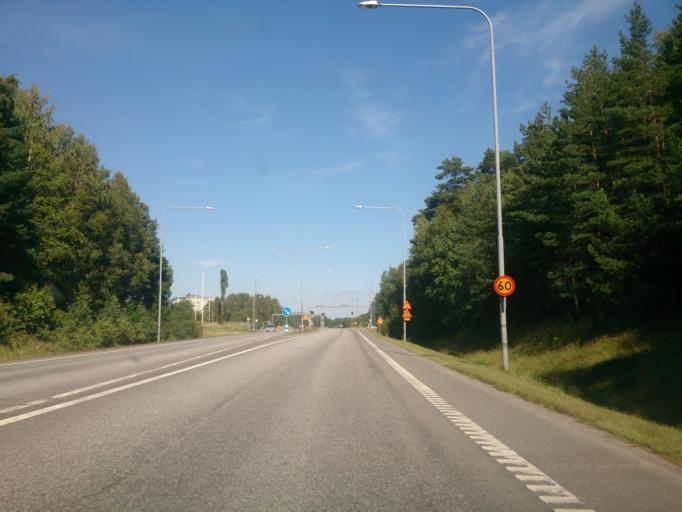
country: SE
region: OEstergoetland
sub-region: Norrkopings Kommun
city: Norrkoping
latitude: 58.5634
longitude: 16.1711
